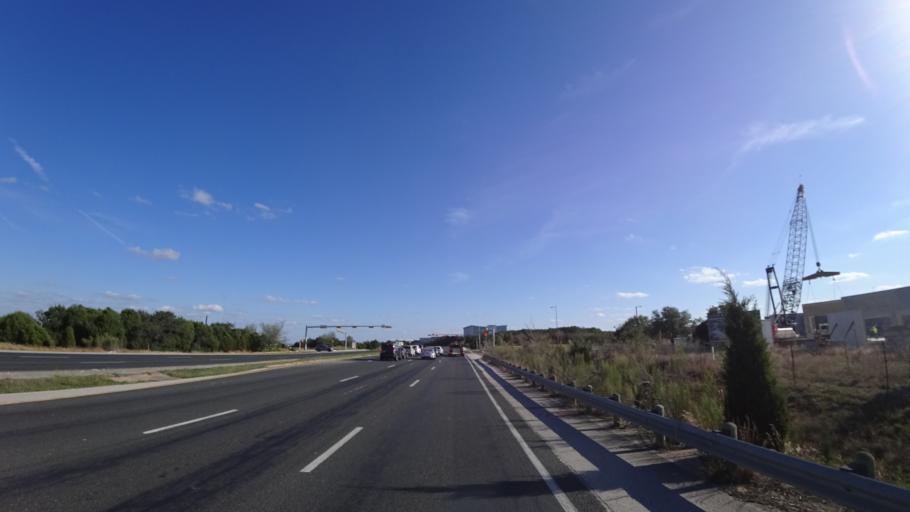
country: US
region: Texas
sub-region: Travis County
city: Barton Creek
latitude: 30.2552
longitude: -97.8665
